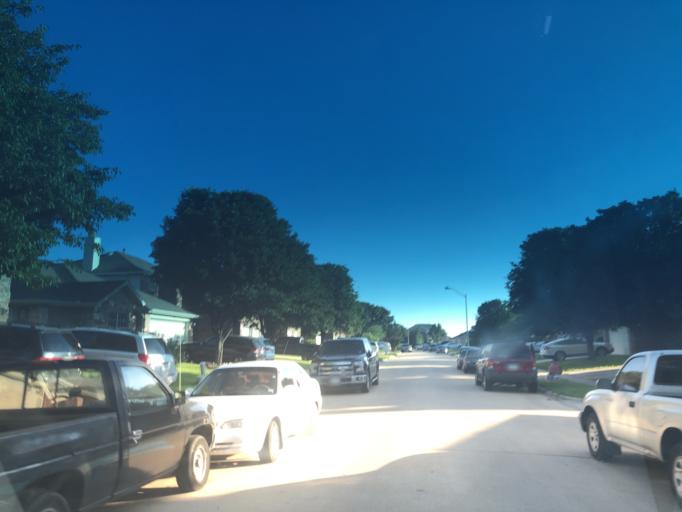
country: US
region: Texas
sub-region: Dallas County
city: Grand Prairie
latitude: 32.6998
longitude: -97.0177
